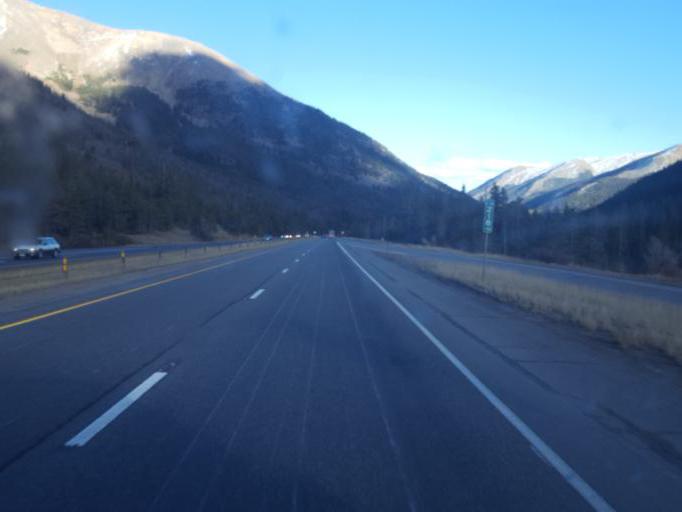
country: US
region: Colorado
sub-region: Clear Creek County
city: Georgetown
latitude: 39.7017
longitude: -105.8559
